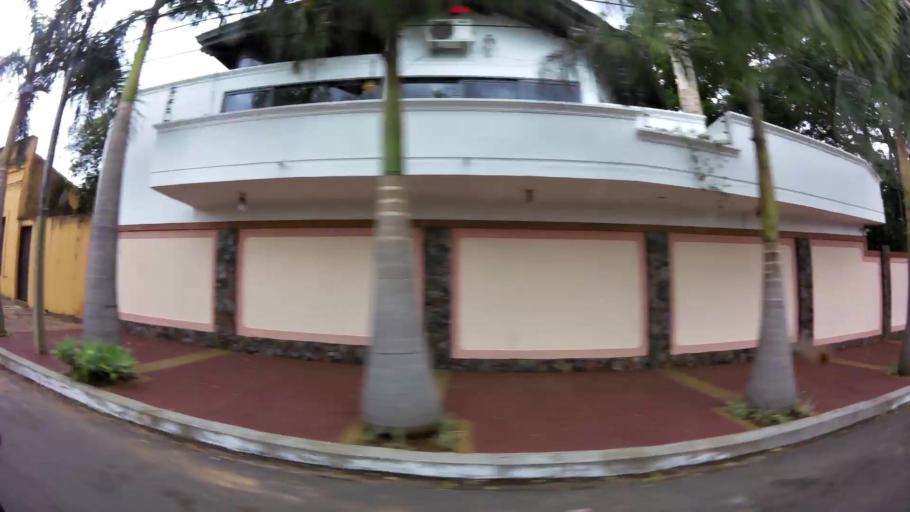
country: PY
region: Central
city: San Lorenzo
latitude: -25.2644
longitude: -57.4949
